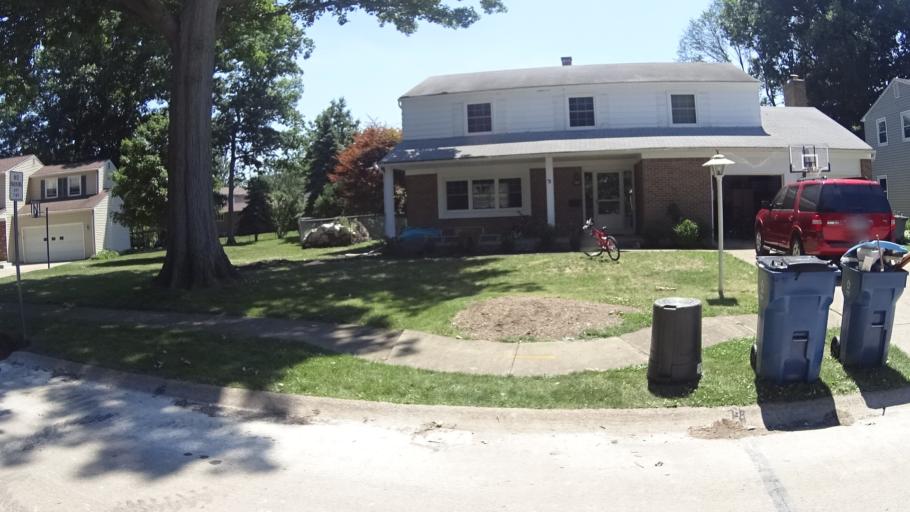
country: US
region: Ohio
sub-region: Erie County
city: Huron
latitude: 41.3961
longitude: -82.5621
